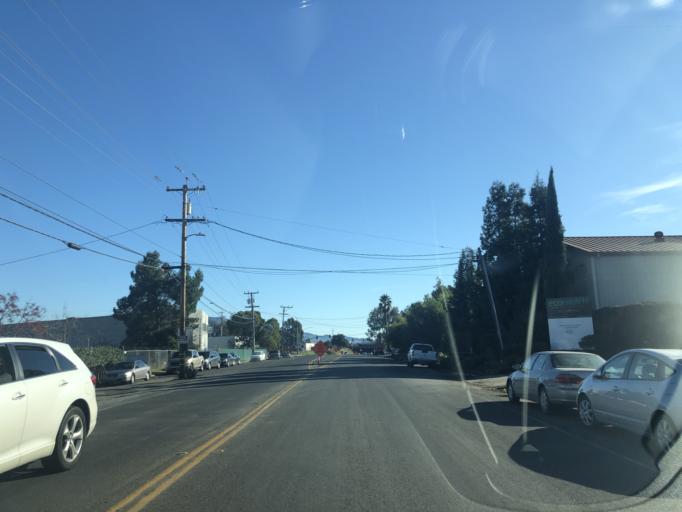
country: US
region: California
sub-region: Contra Costa County
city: Pacheco
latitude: 37.9961
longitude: -122.0760
